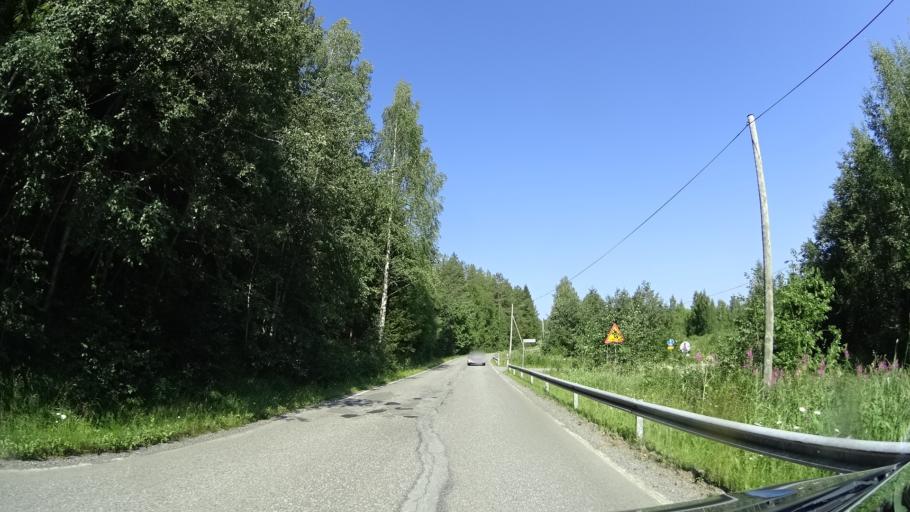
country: FI
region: North Karelia
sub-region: Pielisen Karjala
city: Lieksa
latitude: 63.1167
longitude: 29.7987
